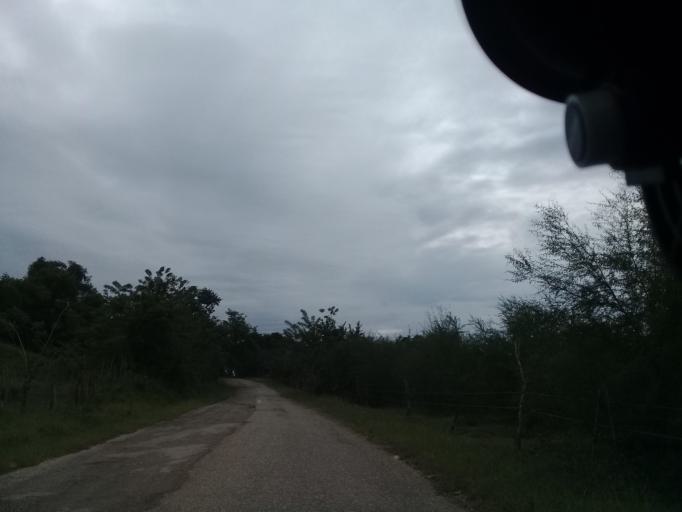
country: MX
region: Veracruz
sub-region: Chalma
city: San Pedro Coyutla
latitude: 21.2136
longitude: -98.3787
